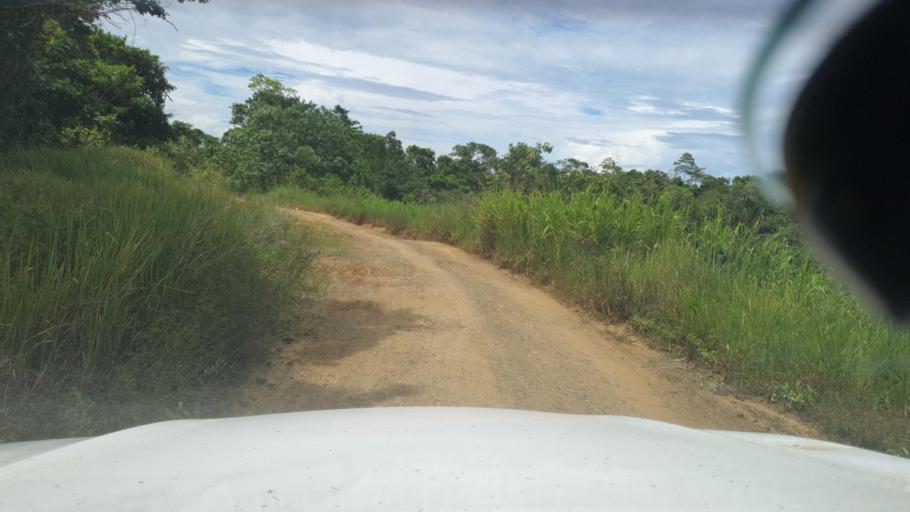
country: SB
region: Guadalcanal
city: Honiara
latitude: -9.4849
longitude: 160.3334
